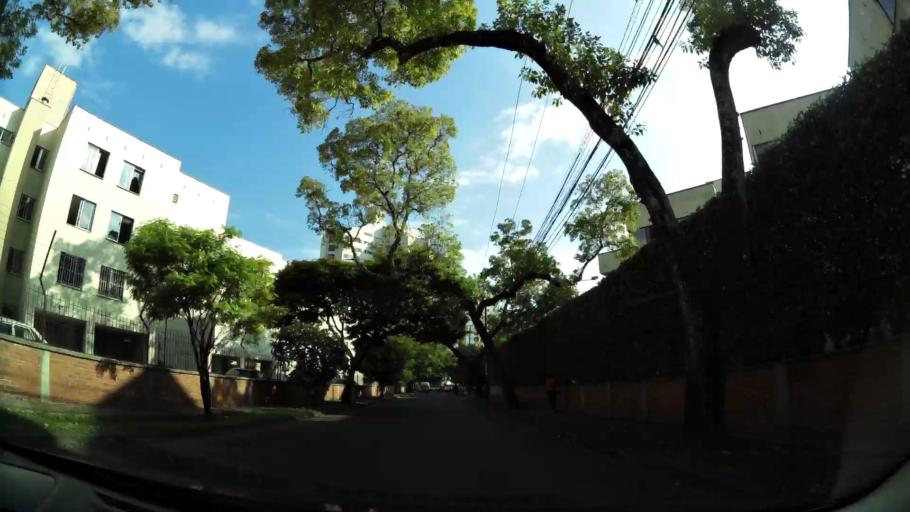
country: CO
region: Valle del Cauca
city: Cali
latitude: 3.4189
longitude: -76.5426
